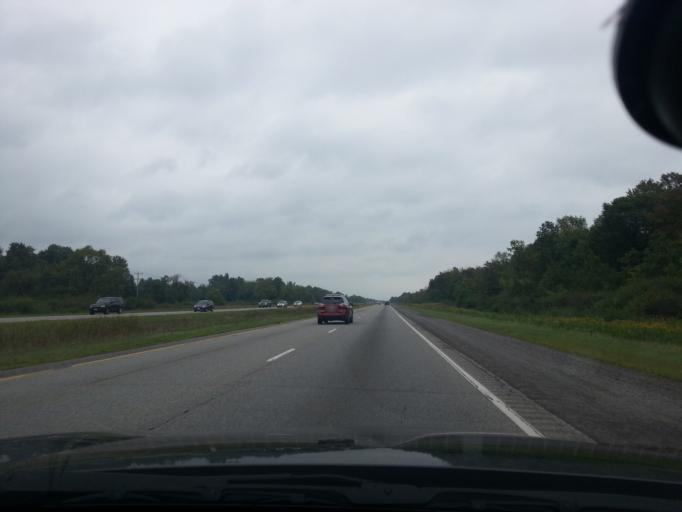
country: CA
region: Ontario
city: Prescott
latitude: 44.6856
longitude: -75.5867
